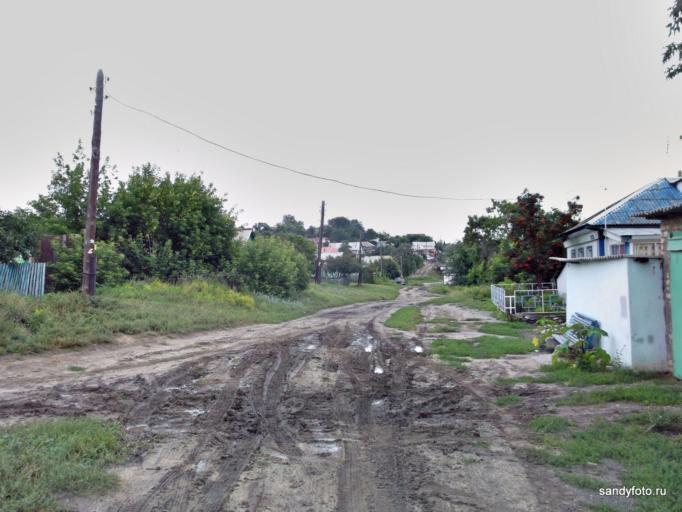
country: RU
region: Chelyabinsk
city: Troitsk
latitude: 54.0984
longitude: 61.5476
